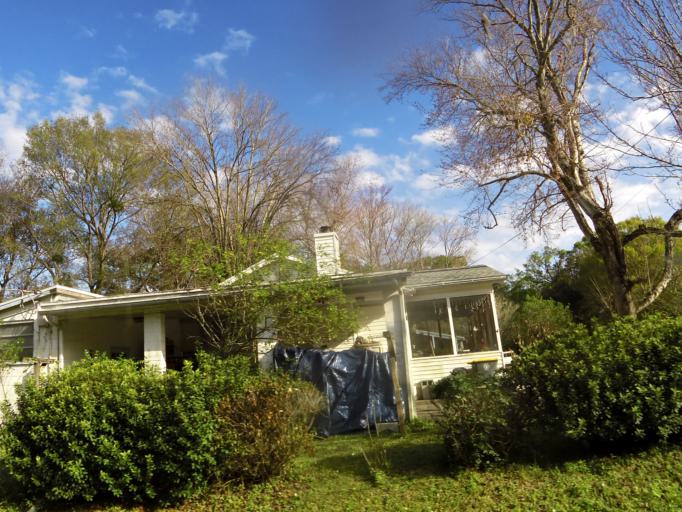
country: US
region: Florida
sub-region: Duval County
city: Jacksonville
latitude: 30.2940
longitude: -81.6241
